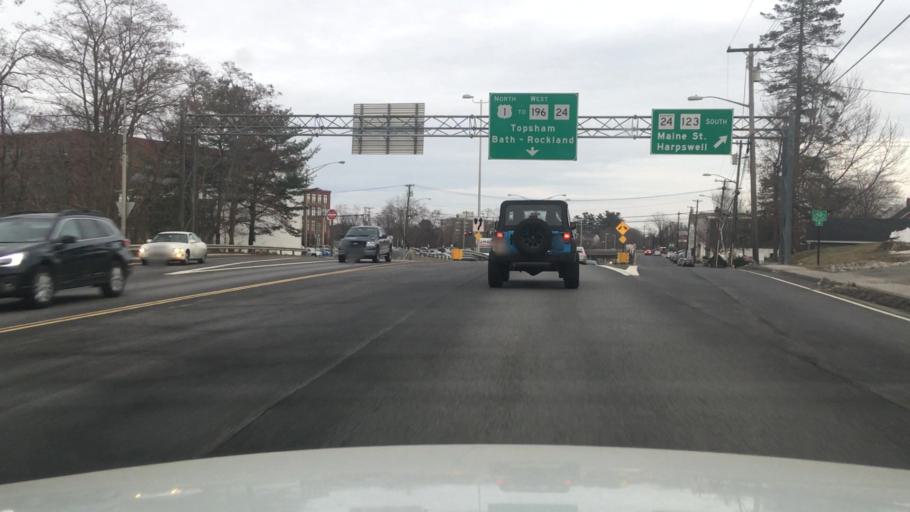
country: US
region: Maine
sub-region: Cumberland County
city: Brunswick
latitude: 43.9177
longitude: -69.9701
